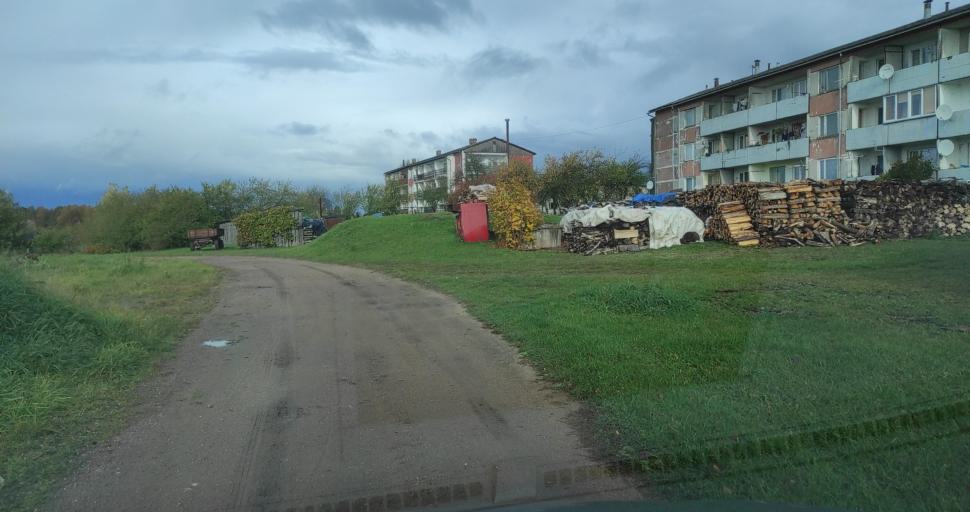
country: LV
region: Vainode
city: Vainode
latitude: 56.5686
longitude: 21.8975
